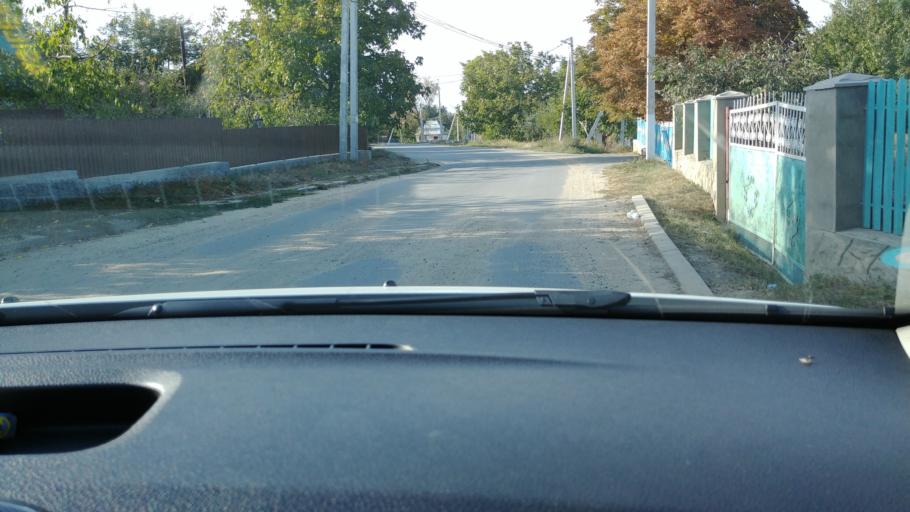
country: MD
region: Rezina
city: Rezina
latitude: 47.7494
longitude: 28.8821
